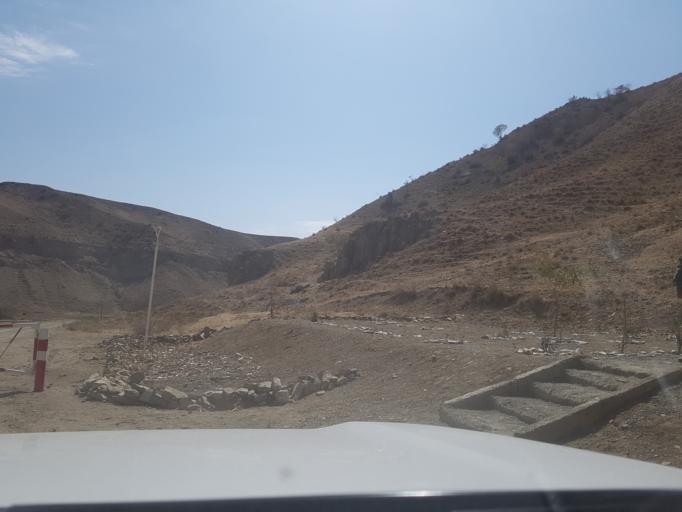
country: TM
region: Ahal
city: Baharly
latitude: 38.2368
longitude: 56.8935
